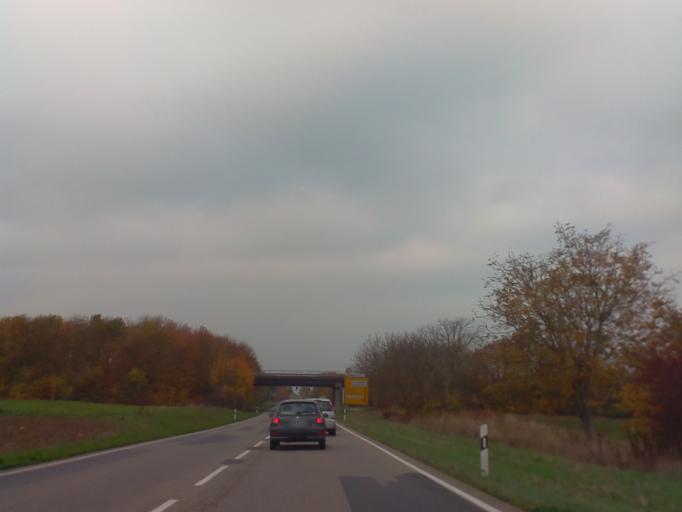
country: DE
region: Baden-Wuerttemberg
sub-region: Karlsruhe Region
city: Ladenburg
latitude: 49.4847
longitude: 8.6045
